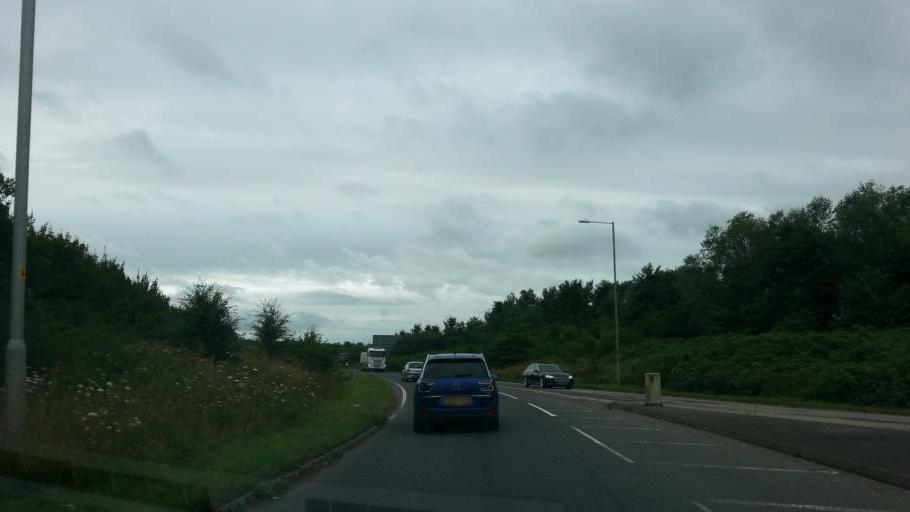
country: GB
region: England
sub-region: Wiltshire
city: Melksham
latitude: 51.3542
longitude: -2.1378
